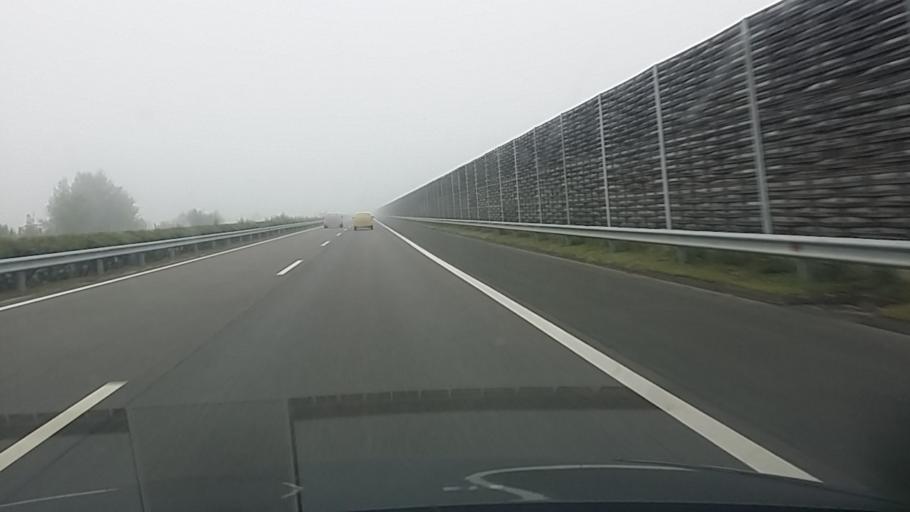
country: HU
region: Csongrad
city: Domaszek
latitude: 46.2745
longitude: 20.0402
